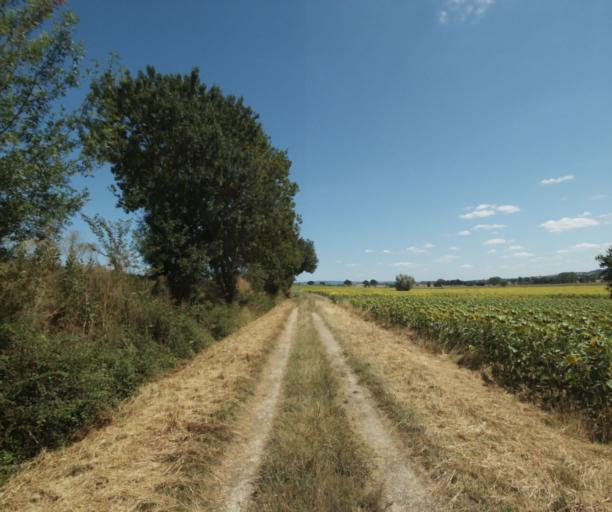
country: FR
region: Midi-Pyrenees
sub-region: Departement de la Haute-Garonne
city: Auriac-sur-Vendinelle
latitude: 43.4982
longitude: 1.8696
